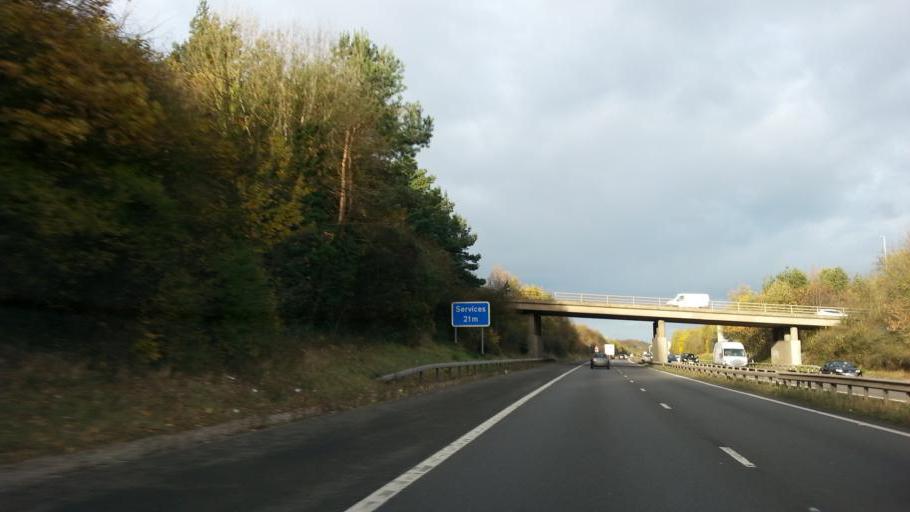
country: GB
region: England
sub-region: Staffordshire
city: Tamworth
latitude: 52.6180
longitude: -1.6314
